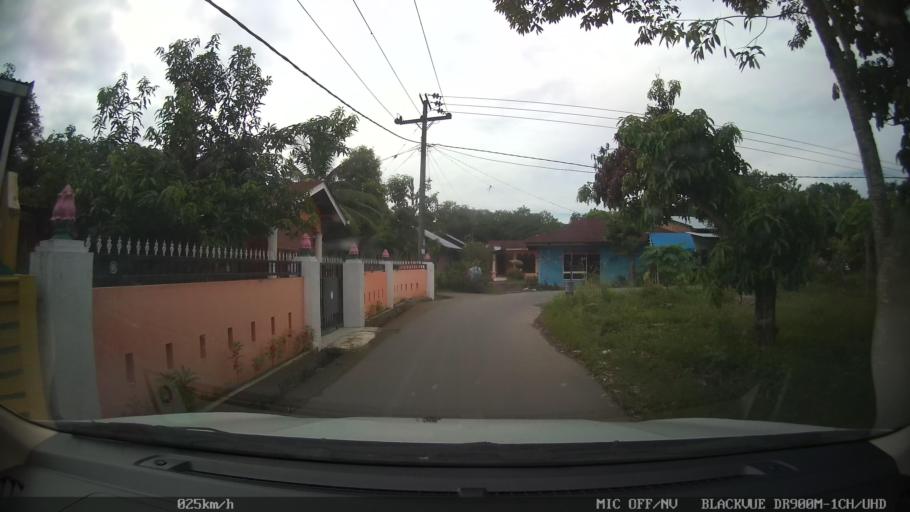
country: ID
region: North Sumatra
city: Sunggal
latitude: 3.6622
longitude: 98.5895
